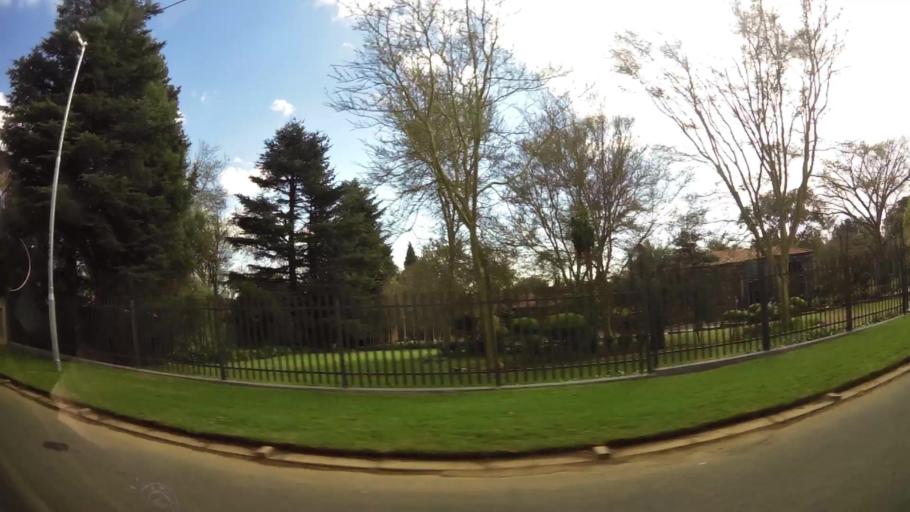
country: ZA
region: Gauteng
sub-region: West Rand District Municipality
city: Muldersdriseloop
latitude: -26.0930
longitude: 27.8559
